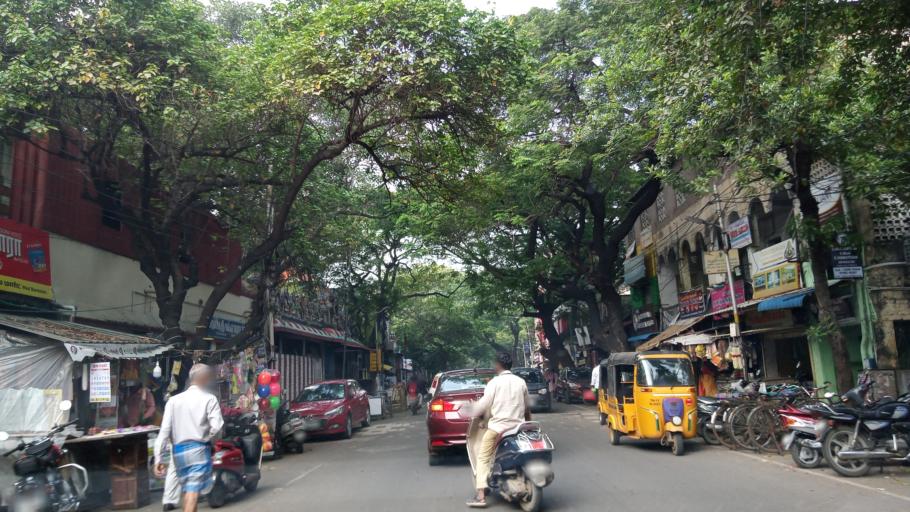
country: IN
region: Tamil Nadu
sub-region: Chennai
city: Chetput
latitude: 13.0405
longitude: 80.2215
